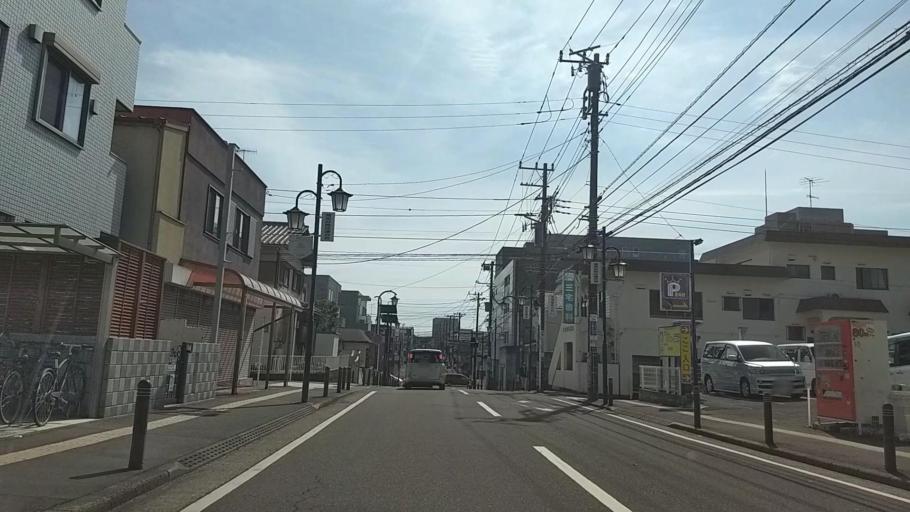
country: JP
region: Kanagawa
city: Fujisawa
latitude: 35.3934
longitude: 139.4660
